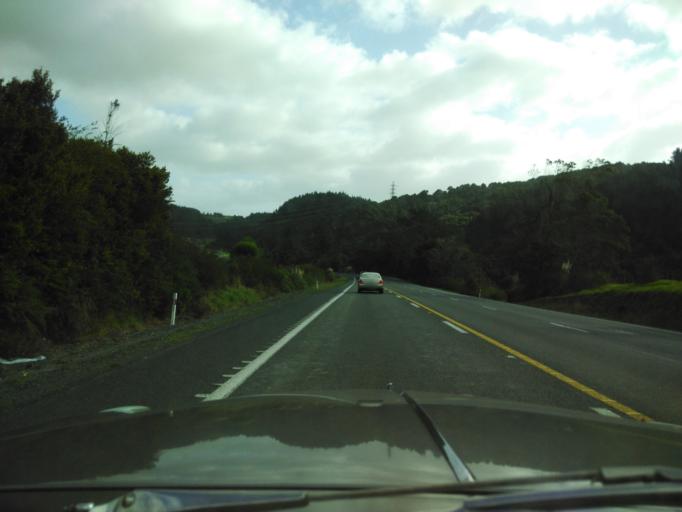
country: NZ
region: Auckland
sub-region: Auckland
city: Wellsford
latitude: -36.2120
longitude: 174.4761
